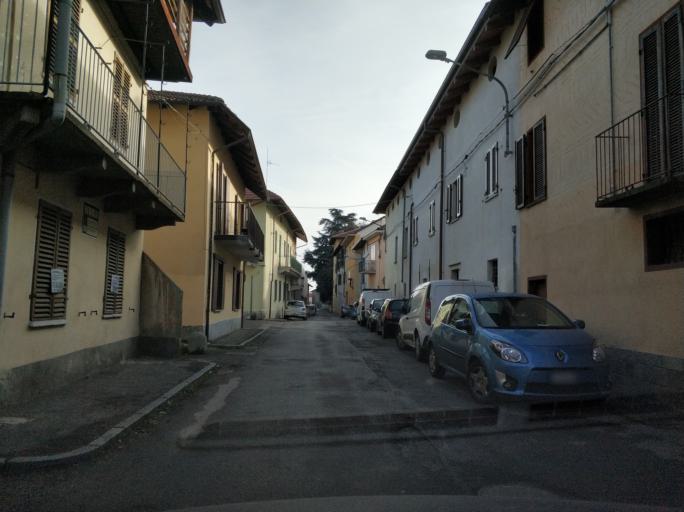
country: IT
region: Piedmont
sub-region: Provincia di Torino
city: Mathi
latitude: 45.2579
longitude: 7.5443
